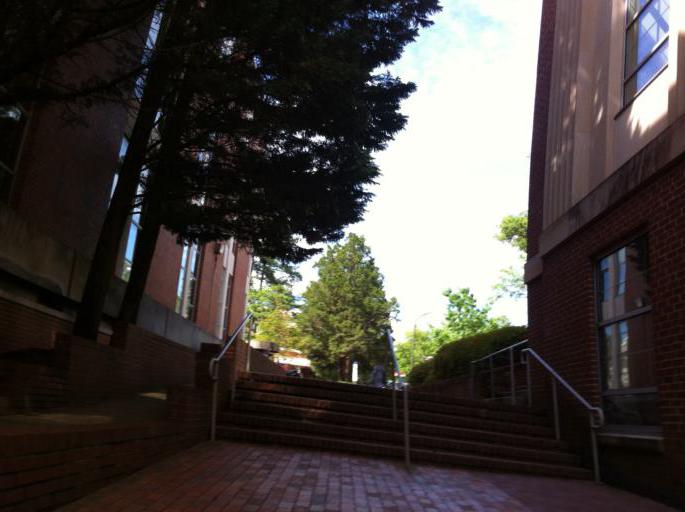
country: US
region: North Carolina
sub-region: Wake County
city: West Raleigh
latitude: 35.7849
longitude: -78.6689
